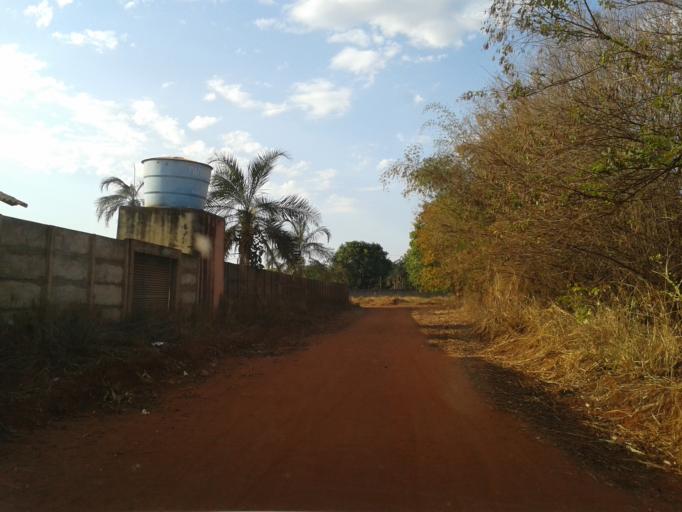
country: BR
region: Minas Gerais
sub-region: Ituiutaba
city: Ituiutaba
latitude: -18.9977
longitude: -49.4356
